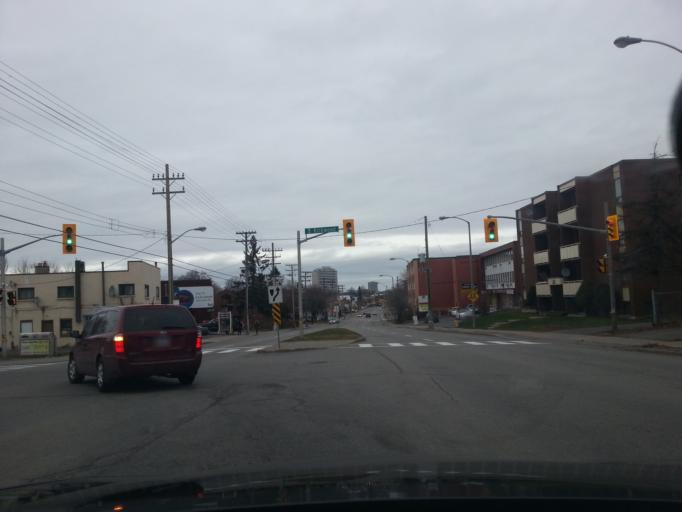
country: CA
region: Ontario
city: Ottawa
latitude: 45.3771
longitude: -75.7332
